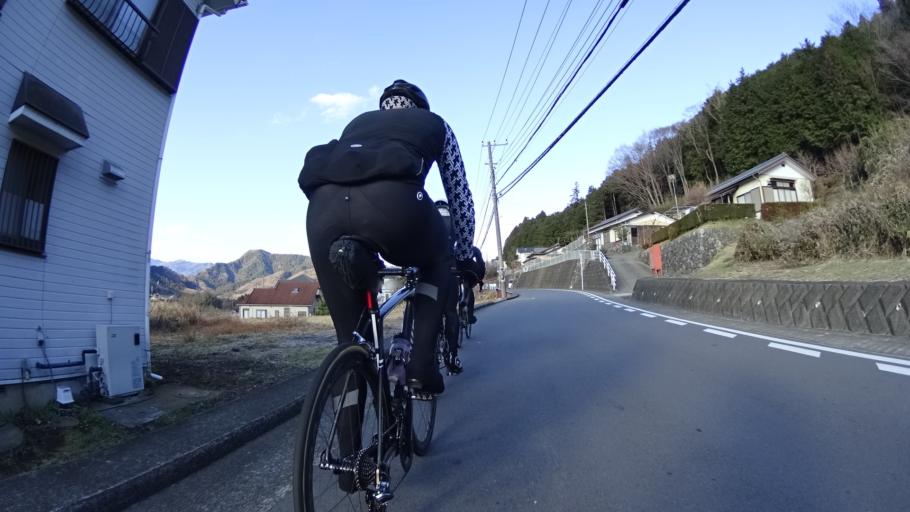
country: JP
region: Tokyo
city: Hachioji
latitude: 35.5684
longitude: 139.2560
